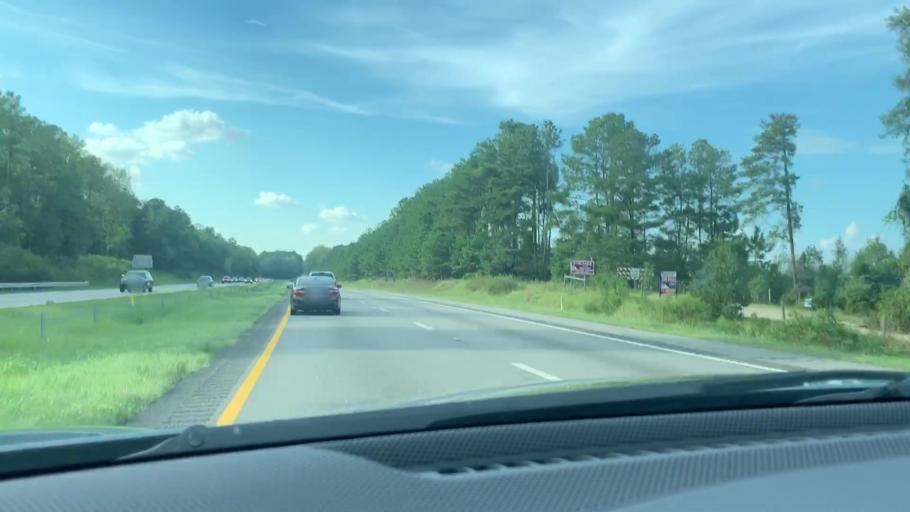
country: US
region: South Carolina
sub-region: Orangeburg County
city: Brookdale
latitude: 33.4617
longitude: -80.7342
